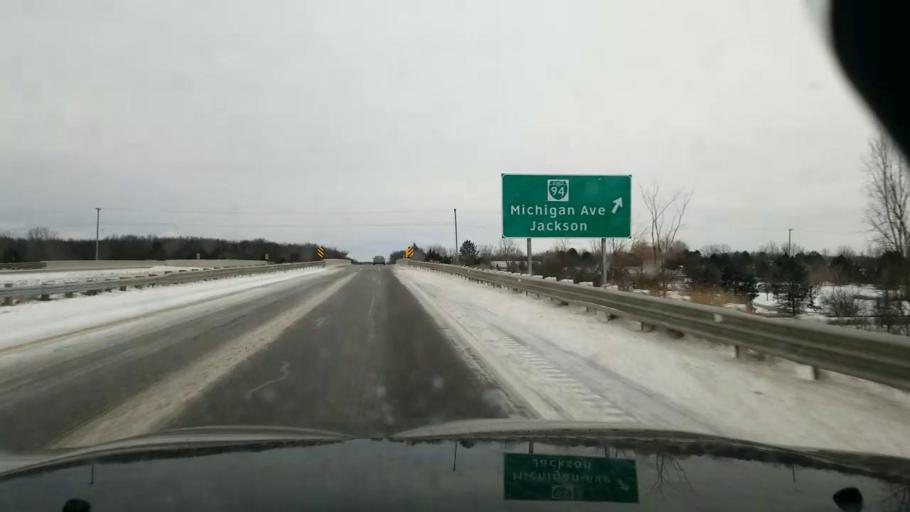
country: US
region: Michigan
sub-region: Jackson County
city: Jackson
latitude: 42.2560
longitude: -84.4765
